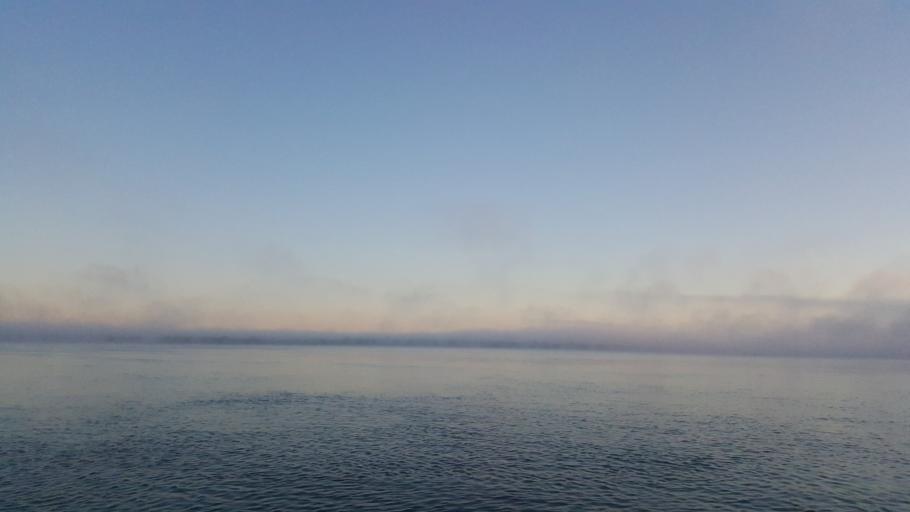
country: AR
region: Corrientes
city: Ituzaingo
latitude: -27.5961
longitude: -56.7161
